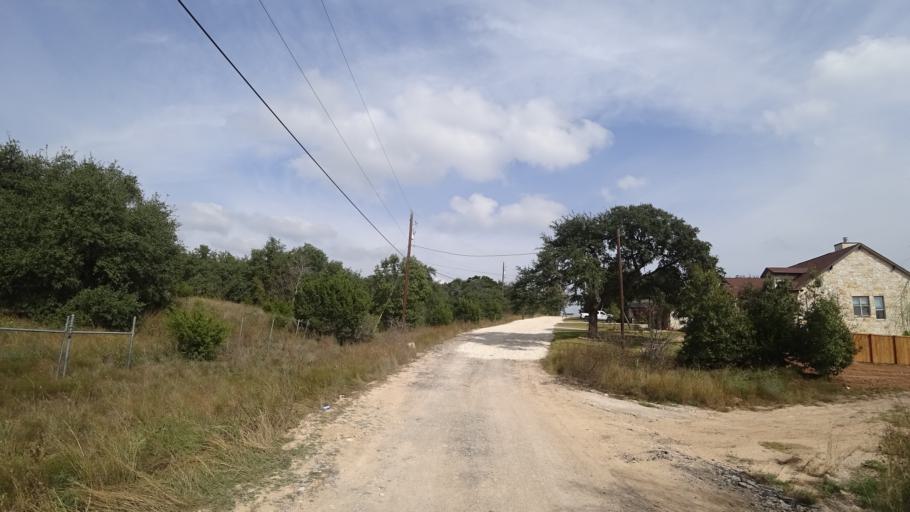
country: US
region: Texas
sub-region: Travis County
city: Hudson Bend
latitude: 30.3885
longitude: -97.9395
